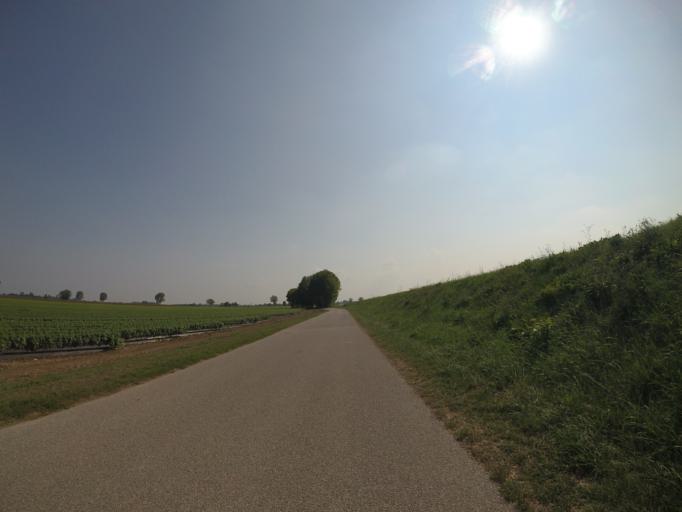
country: IT
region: Friuli Venezia Giulia
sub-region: Provincia di Udine
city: Camino al Tagliamento
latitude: 45.9294
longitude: 12.9226
